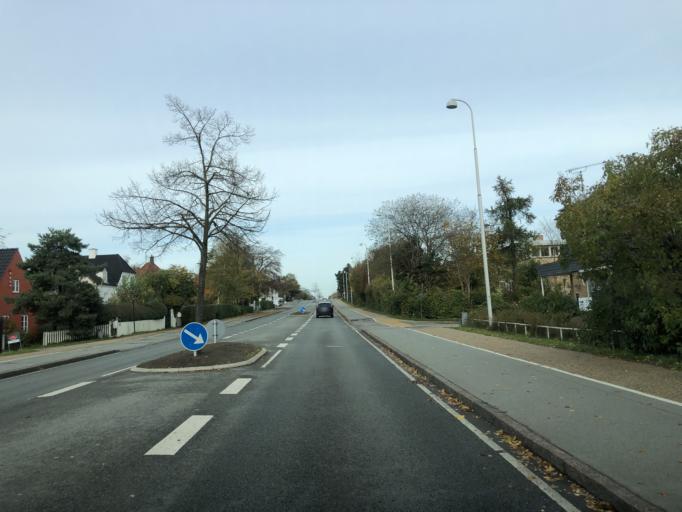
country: DK
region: Capital Region
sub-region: Rudersdal Kommune
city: Birkerod
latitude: 55.8456
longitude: 12.4316
